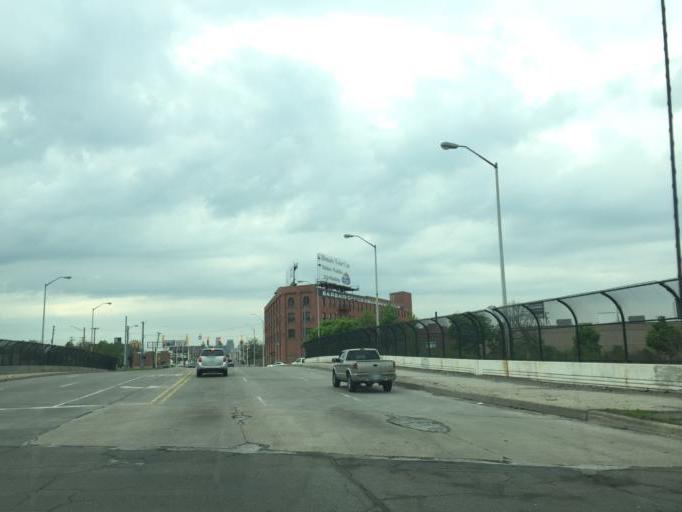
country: US
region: Michigan
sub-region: Wayne County
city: Highland Park
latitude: 42.3515
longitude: -83.0964
